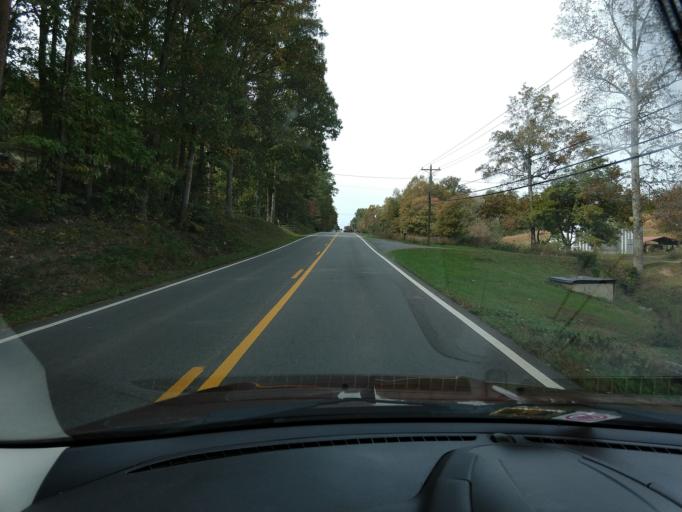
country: US
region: Virginia
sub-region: Pittsylvania County
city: Gretna
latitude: 36.9540
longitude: -79.3893
